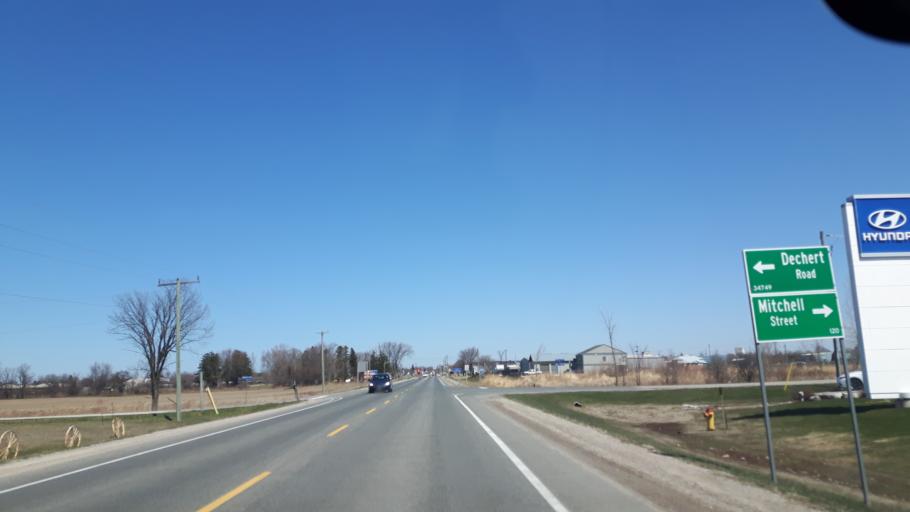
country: CA
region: Ontario
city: Goderich
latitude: 43.7220
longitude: -81.7057
